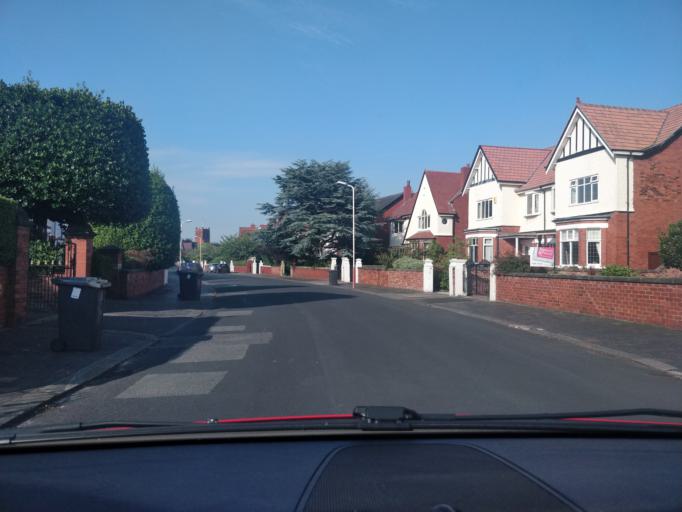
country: GB
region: England
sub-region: Sefton
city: Southport
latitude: 53.6570
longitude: -2.9803
